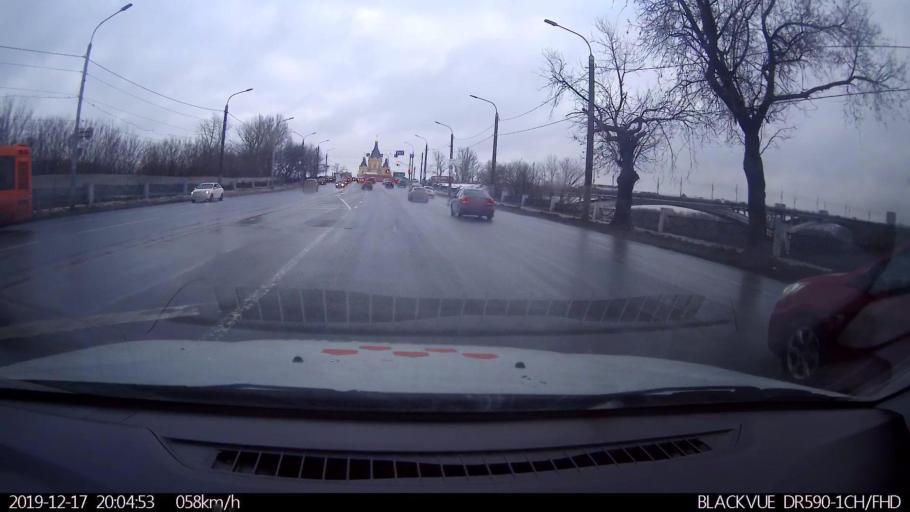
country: RU
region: Nizjnij Novgorod
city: Nizhniy Novgorod
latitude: 56.3270
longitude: 43.9683
